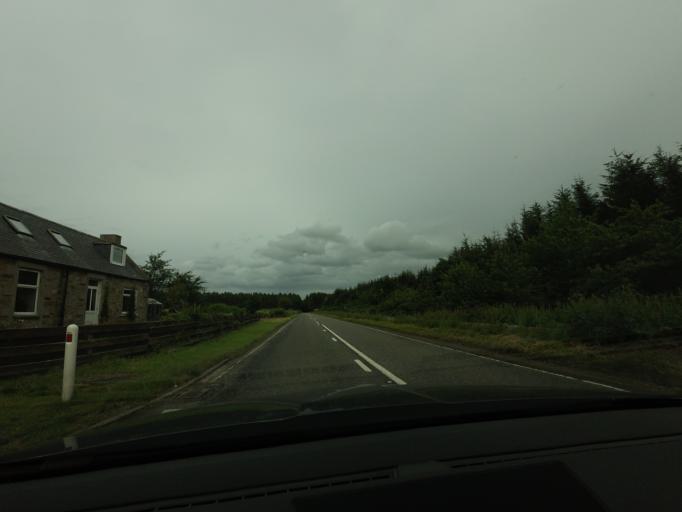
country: GB
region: Scotland
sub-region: Moray
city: Findochty
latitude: 57.6759
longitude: -2.9048
